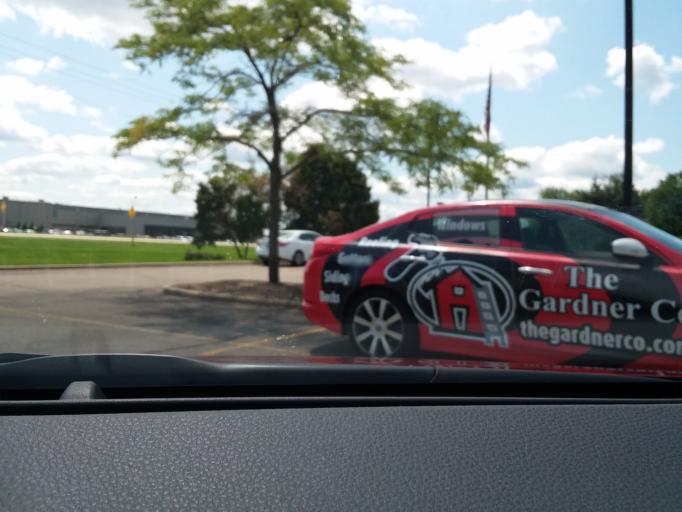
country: US
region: Wisconsin
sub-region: Dane County
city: Windsor
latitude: 43.1954
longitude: -89.3337
